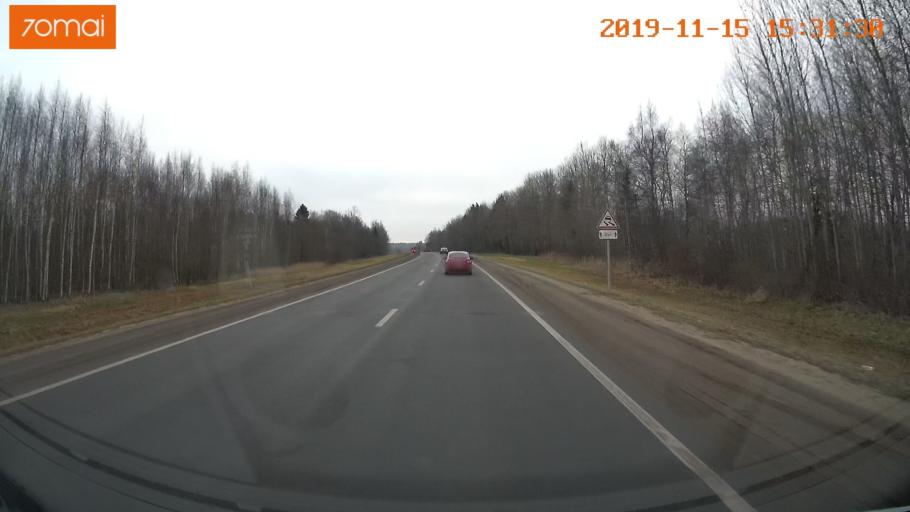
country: RU
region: Jaroslavl
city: Danilov
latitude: 58.0996
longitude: 40.1069
